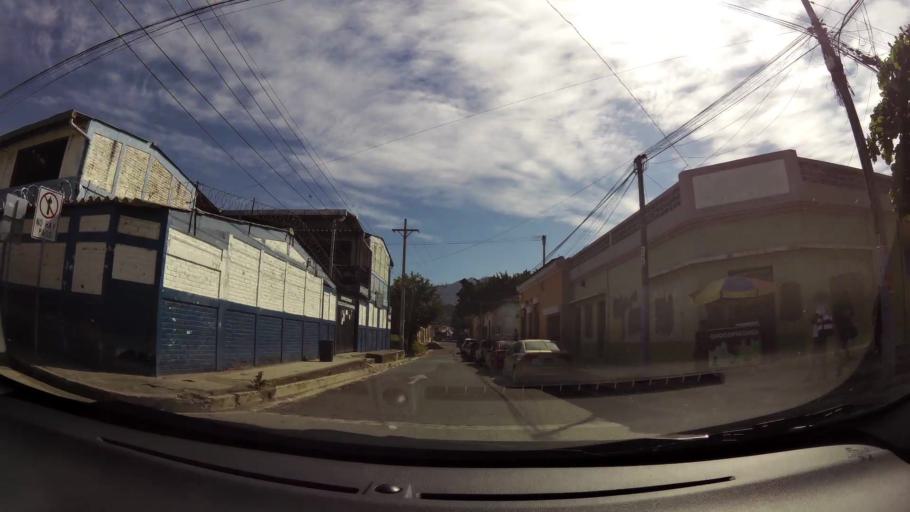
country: SV
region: Santa Ana
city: Chalchuapa
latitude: 13.9871
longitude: -89.6806
